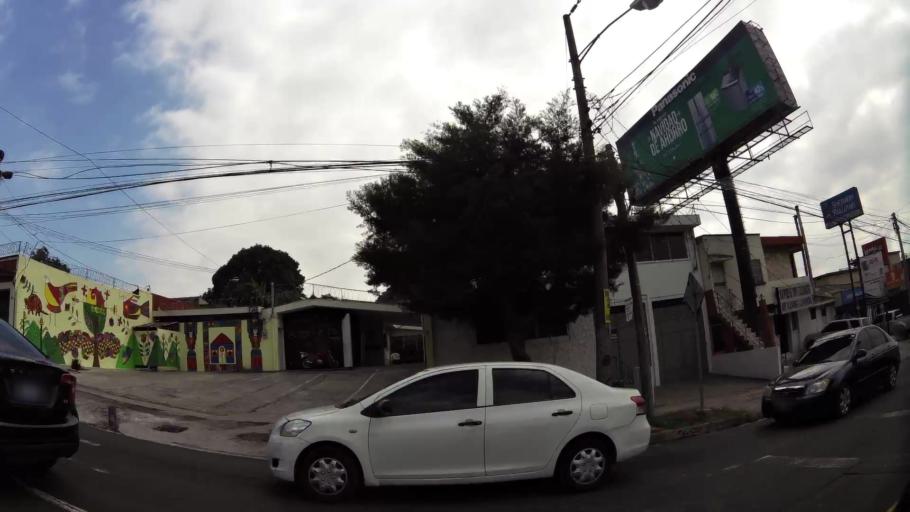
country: SV
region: La Libertad
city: Antiguo Cuscatlan
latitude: 13.7062
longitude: -89.2492
